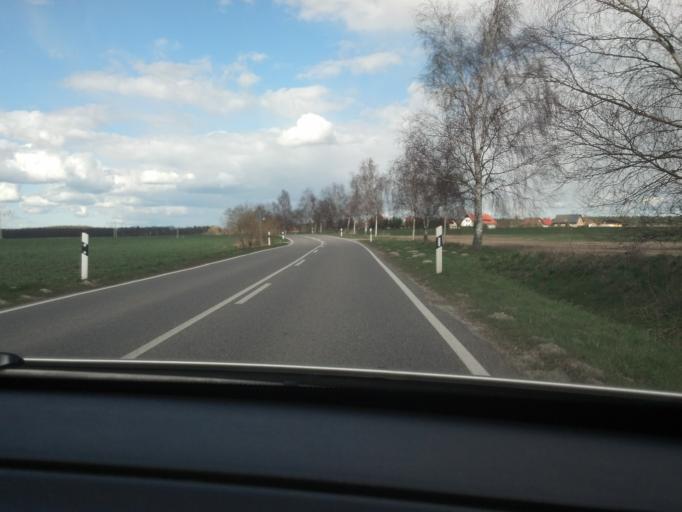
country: DE
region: Mecklenburg-Vorpommern
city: Burg Stargard
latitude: 53.5150
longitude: 13.3170
